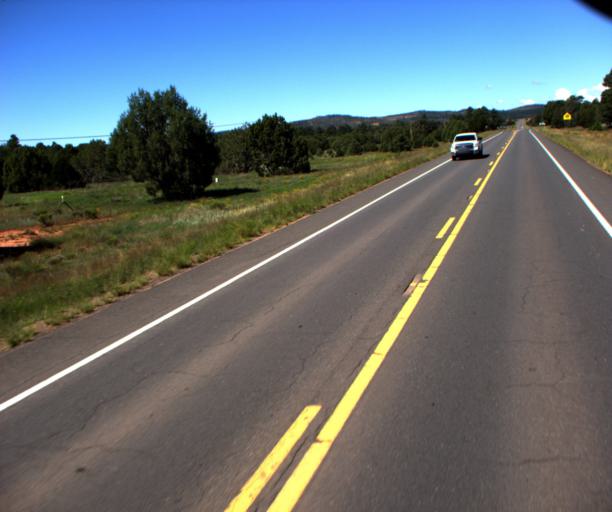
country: US
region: Arizona
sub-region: Navajo County
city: Linden
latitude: 34.2854
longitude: -110.1332
